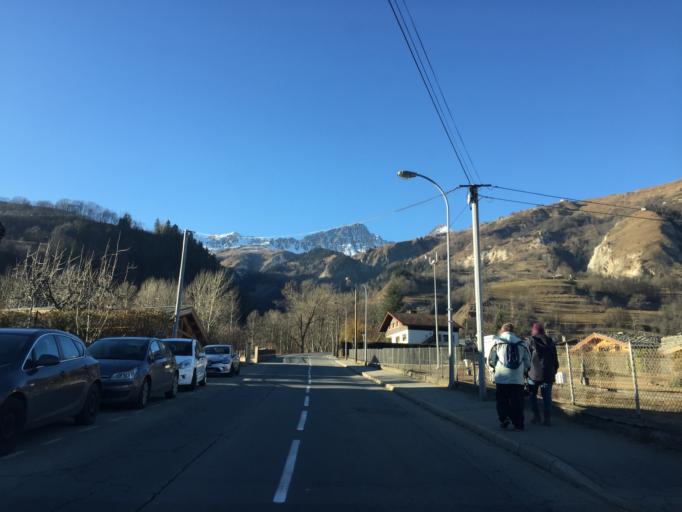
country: FR
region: Rhone-Alpes
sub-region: Departement de la Savoie
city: Bourg-Saint-Maurice
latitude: 45.6124
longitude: 6.7637
